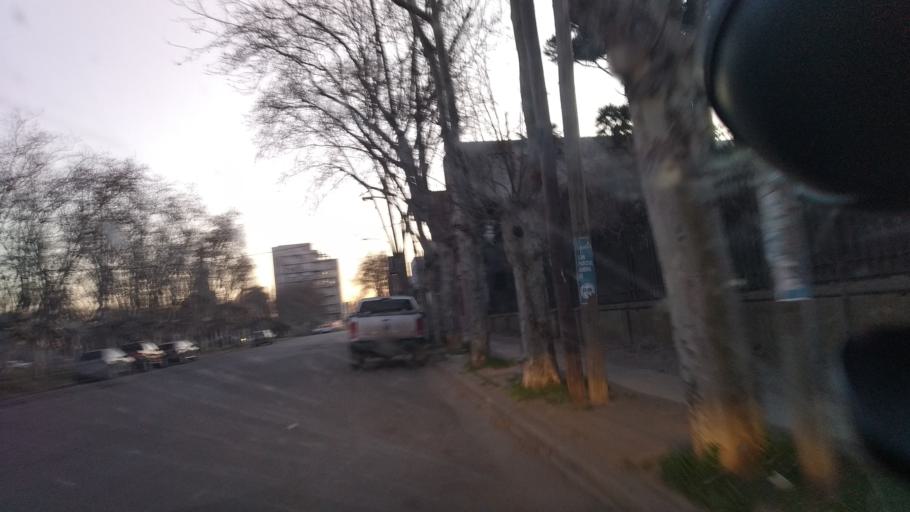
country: AR
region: Buenos Aires
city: Necochea
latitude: -38.5529
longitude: -58.7394
